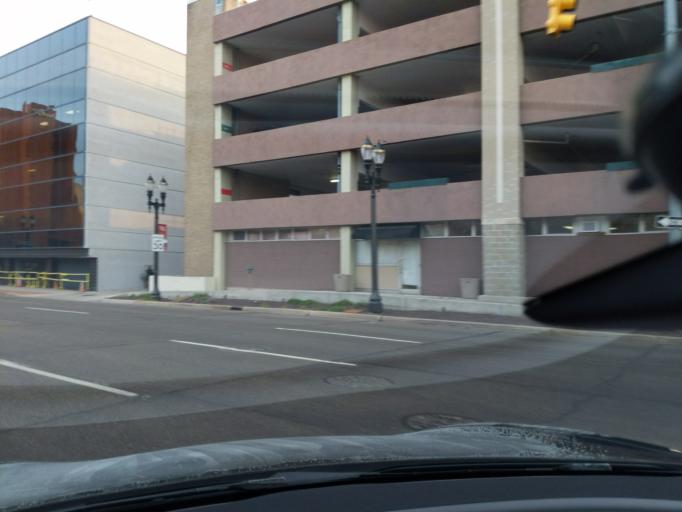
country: US
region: Michigan
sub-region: Ingham County
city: Lansing
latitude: 42.7326
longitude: -84.5507
